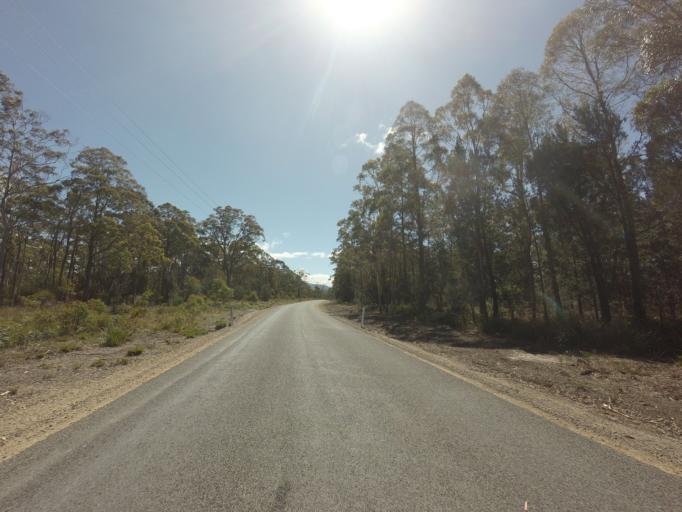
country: AU
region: Tasmania
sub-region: Break O'Day
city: St Helens
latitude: -41.6022
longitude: 148.2049
